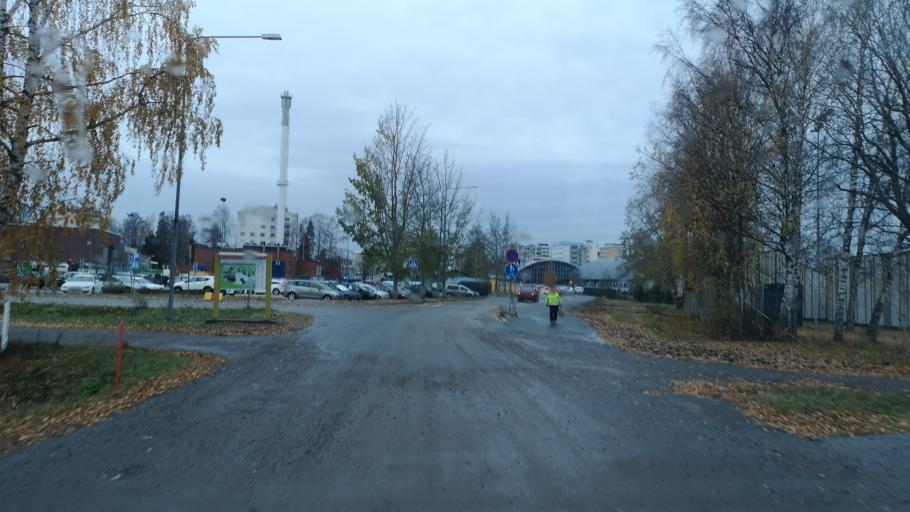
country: FI
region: Ostrobothnia
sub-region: Vaasa
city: Vaasa
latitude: 63.0838
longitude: 21.6202
